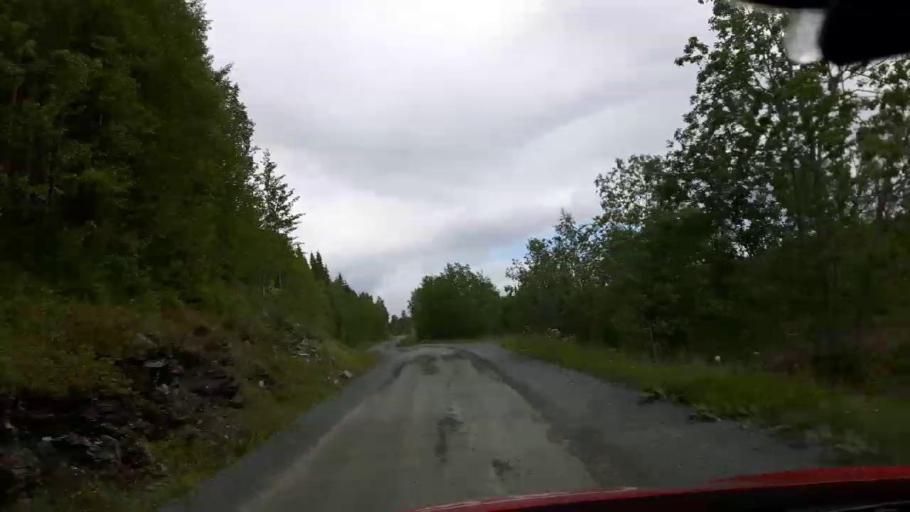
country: NO
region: Nord-Trondelag
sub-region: Lierne
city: Sandvika
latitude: 64.1498
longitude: 13.9692
